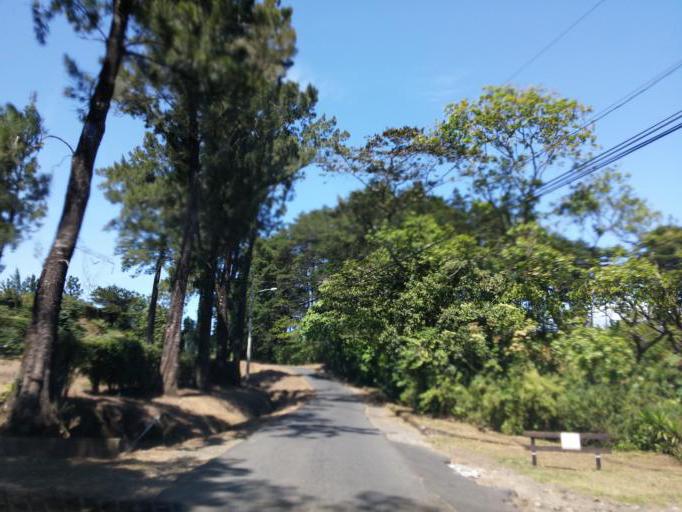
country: CR
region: Heredia
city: Santo Domingo
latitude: 10.0735
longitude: -84.1270
